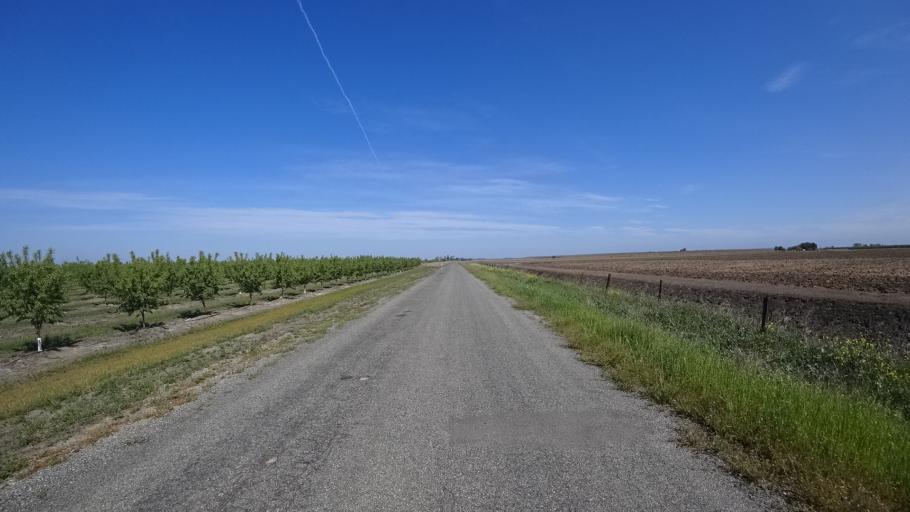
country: US
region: California
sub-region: Glenn County
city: Hamilton City
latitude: 39.6098
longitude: -122.0557
